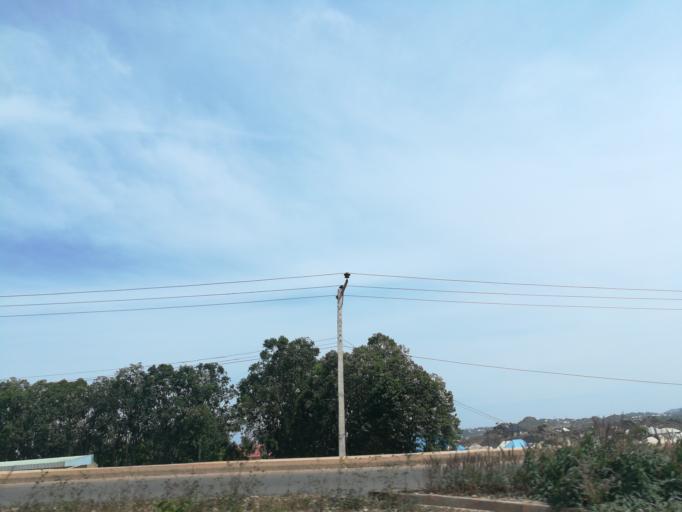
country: NG
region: Plateau
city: Bukuru
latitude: 9.8277
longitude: 8.8667
